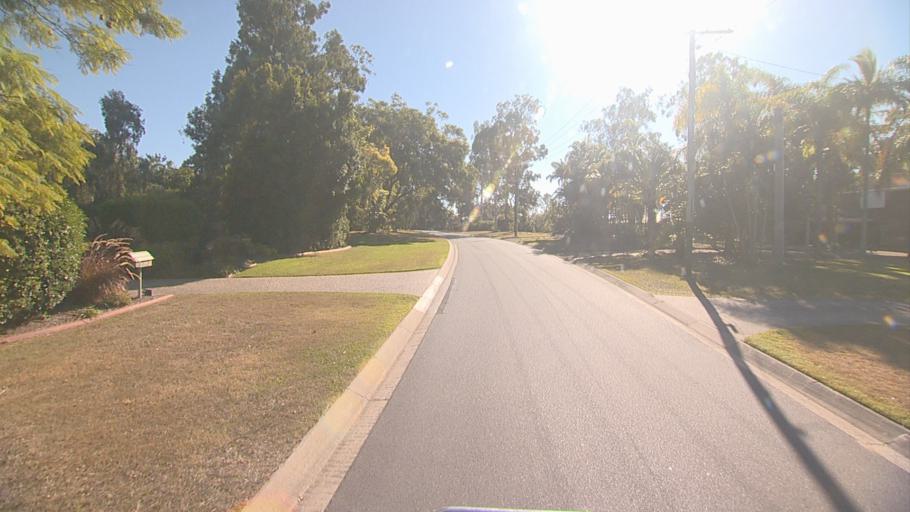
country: AU
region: Queensland
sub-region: Logan
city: Park Ridge South
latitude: -27.6699
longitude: 153.0163
